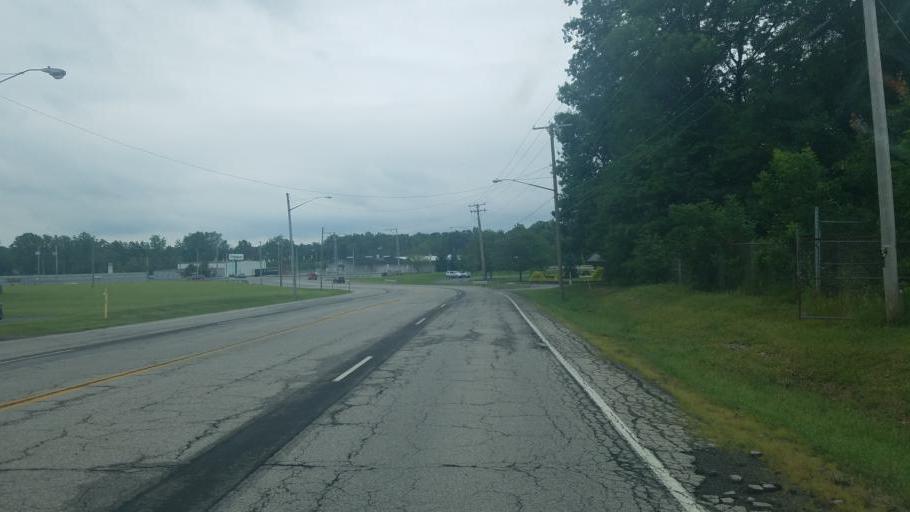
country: US
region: Ohio
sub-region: Richland County
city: Ontario
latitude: 40.7682
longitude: -82.5974
